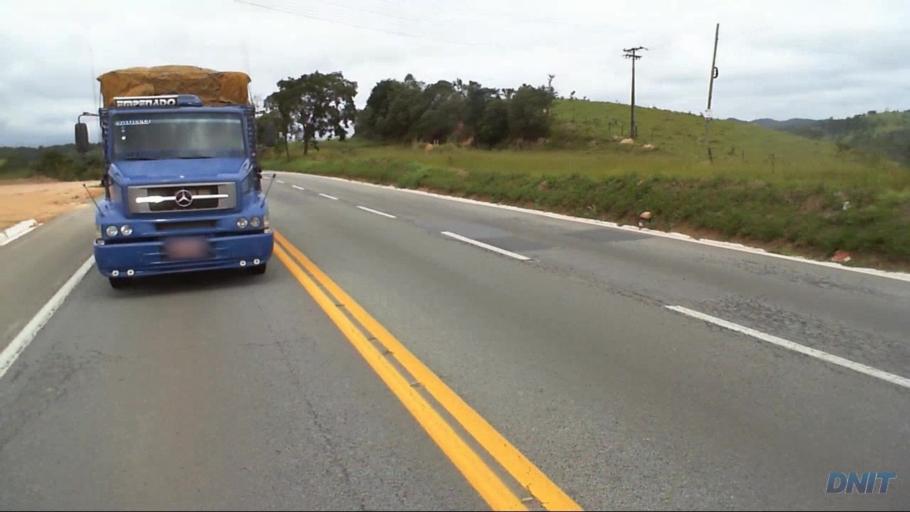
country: BR
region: Minas Gerais
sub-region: Caete
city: Caete
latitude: -19.7332
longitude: -43.5594
